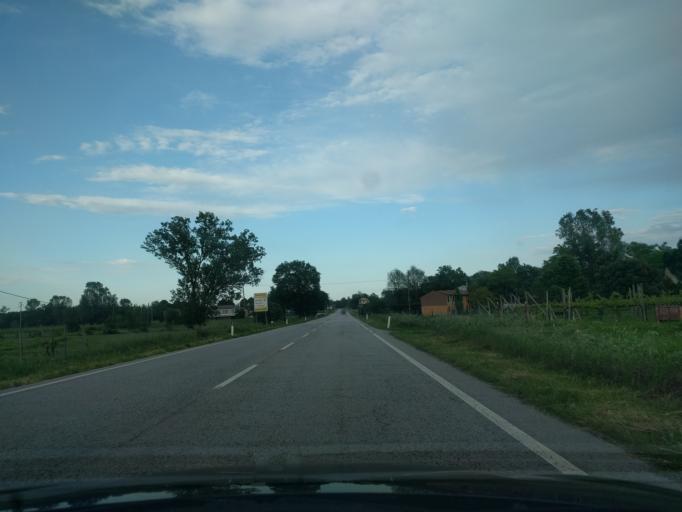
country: IT
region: Veneto
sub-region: Provincia di Rovigo
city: Canaro
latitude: 44.9305
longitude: 11.7150
